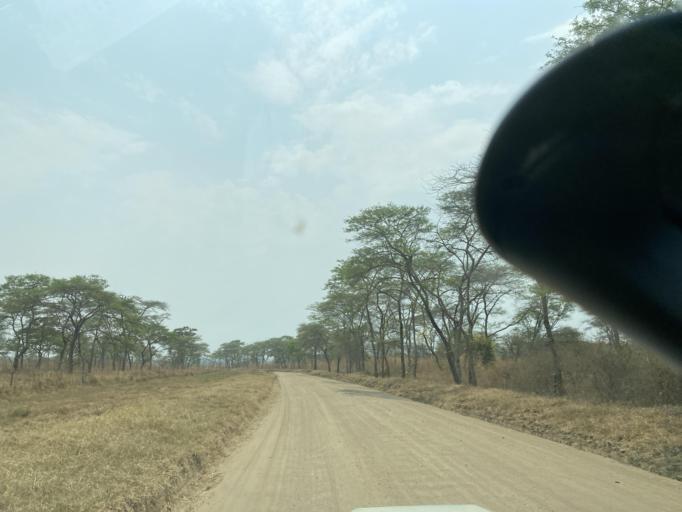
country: ZM
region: Lusaka
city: Kafue
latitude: -15.5863
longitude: 28.1170
